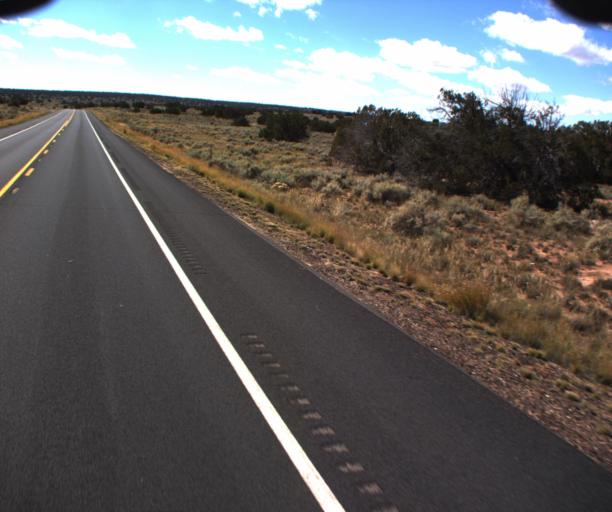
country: US
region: Arizona
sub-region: Apache County
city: Houck
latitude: 35.1734
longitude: -109.3381
